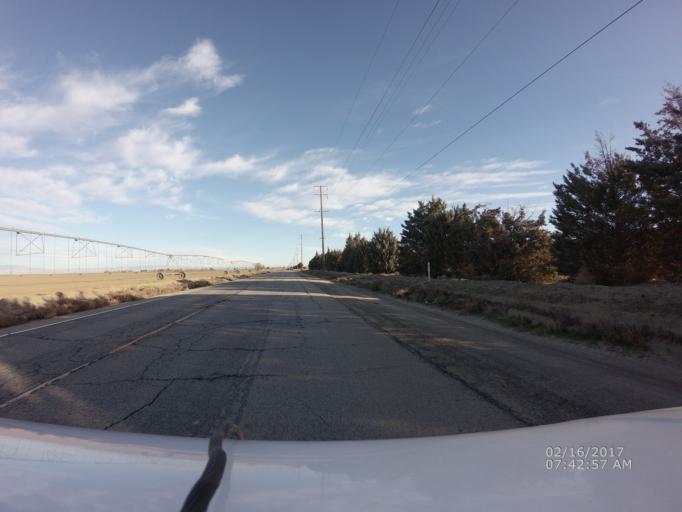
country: US
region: California
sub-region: Los Angeles County
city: Littlerock
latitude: 34.6701
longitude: -117.9697
